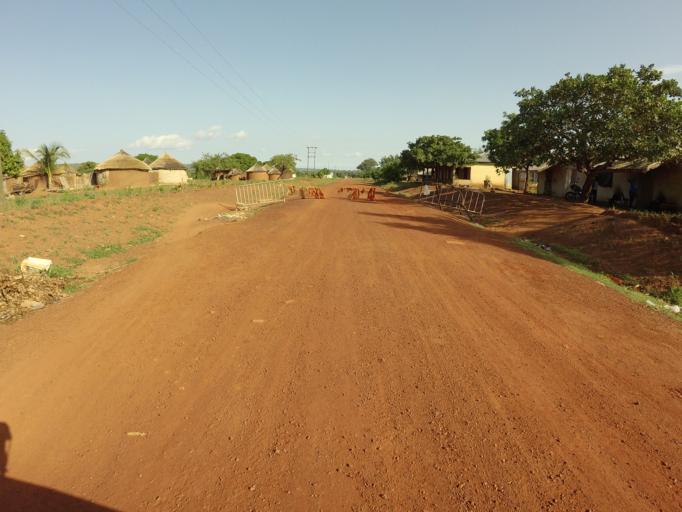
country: GH
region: Upper East
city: Bawku
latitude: 10.6263
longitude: -0.1793
